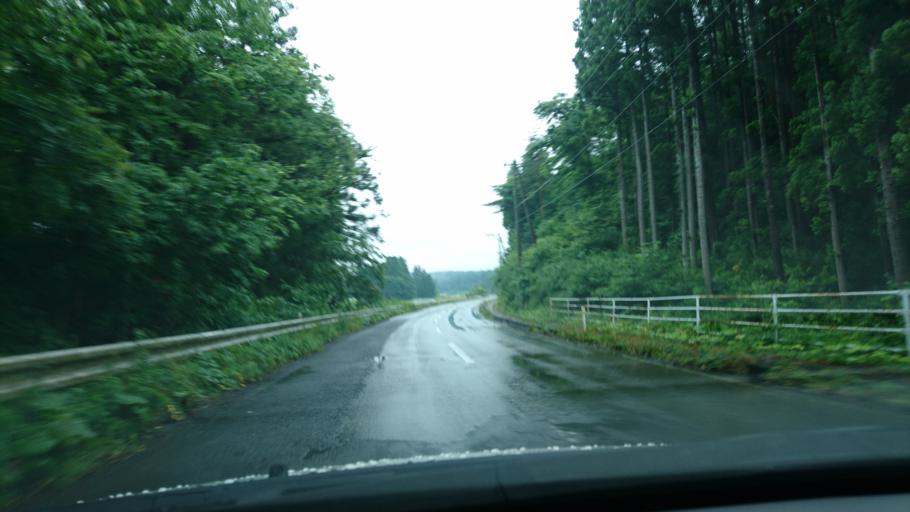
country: JP
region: Iwate
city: Ichinoseki
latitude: 38.9362
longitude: 141.0468
